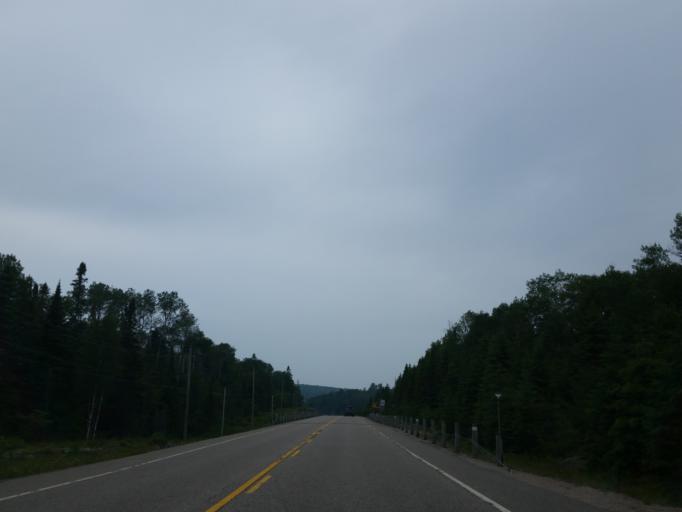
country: CA
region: Ontario
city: Bancroft
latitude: 45.5860
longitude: -78.3783
